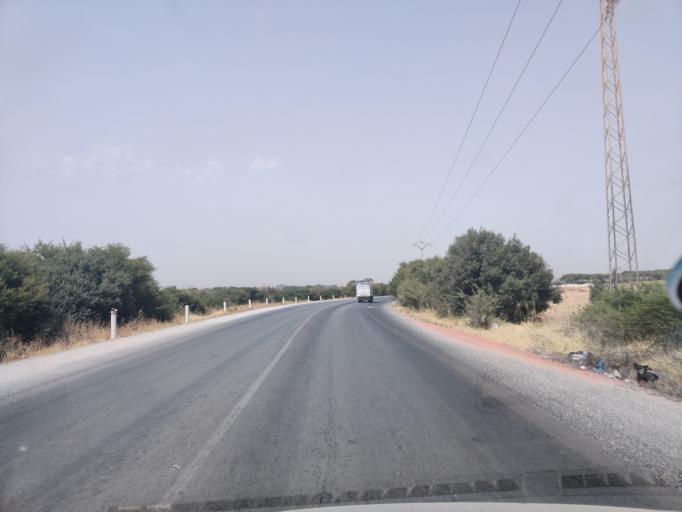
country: TN
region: Tunis
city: La Sebala du Mornag
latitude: 36.6499
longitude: 10.3405
